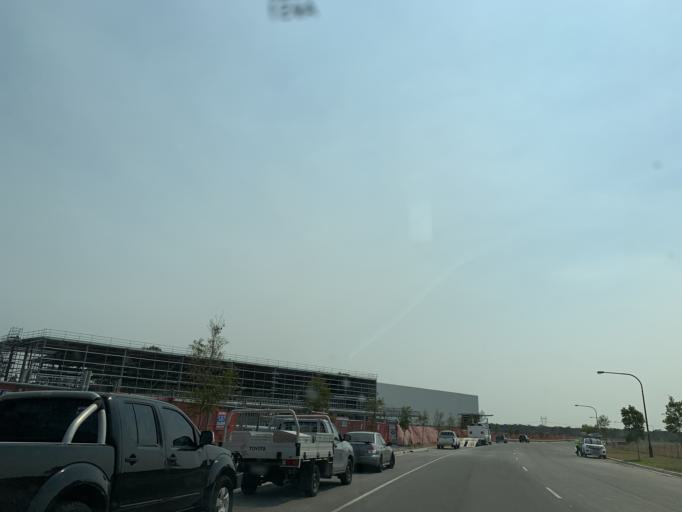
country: AU
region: New South Wales
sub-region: Blacktown
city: Hassall Grove
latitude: -33.7183
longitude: 150.8296
